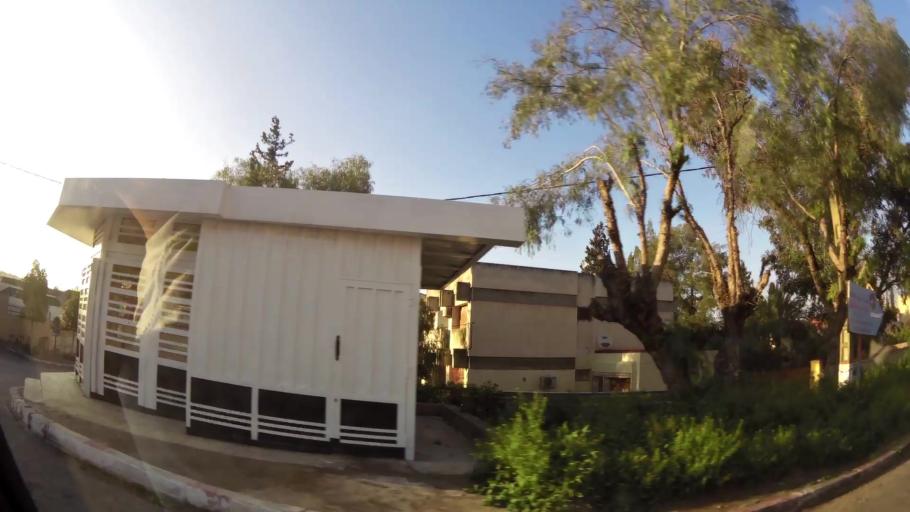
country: MA
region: Chaouia-Ouardigha
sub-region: Settat Province
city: Settat
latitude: 33.0102
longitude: -7.6145
